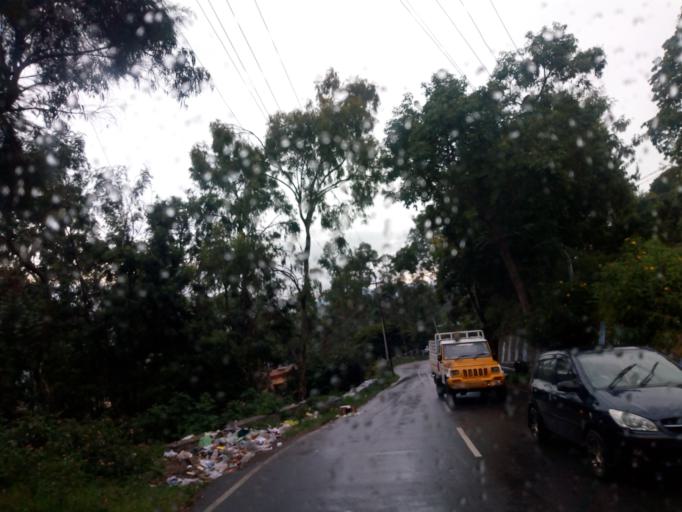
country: IN
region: Tamil Nadu
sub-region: Nilgiri
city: Wellington
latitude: 11.3415
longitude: 76.8030
